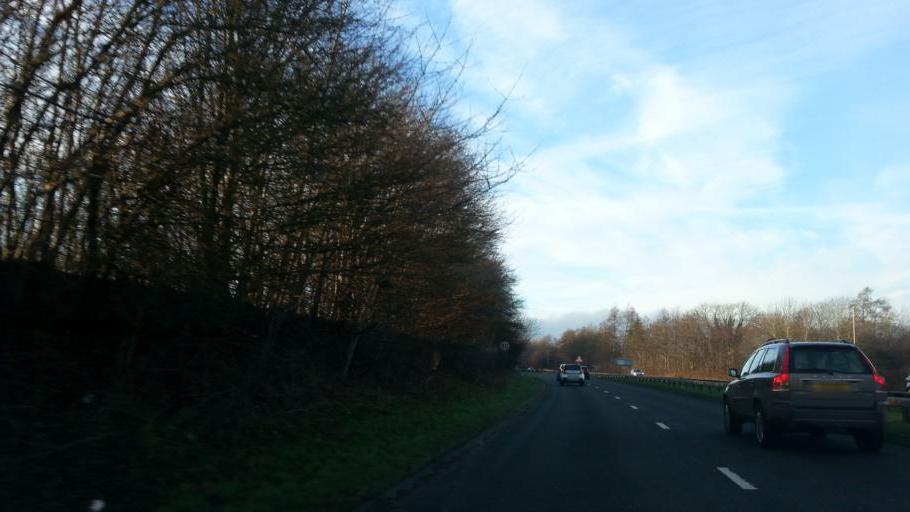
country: GB
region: England
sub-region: Northamptonshire
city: Hardingstone
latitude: 52.2215
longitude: -0.9187
